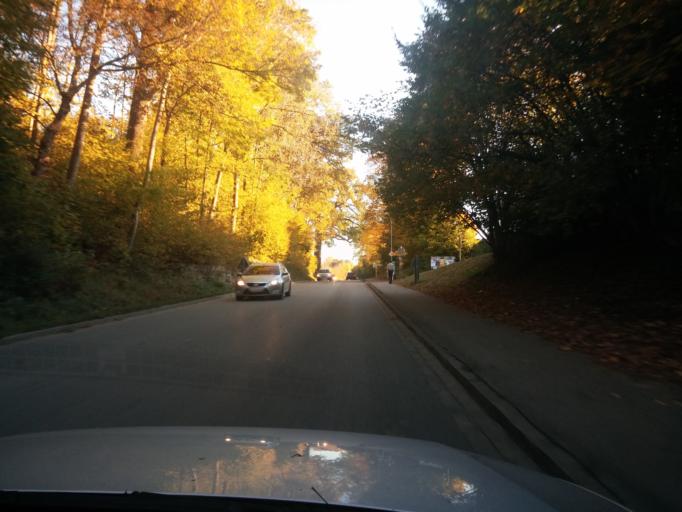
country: DE
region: Bavaria
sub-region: Upper Bavaria
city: Dorfen
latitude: 48.2648
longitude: 12.1565
